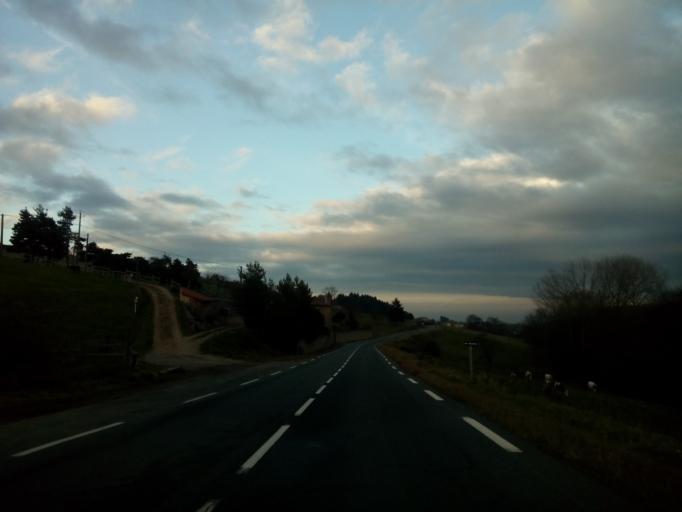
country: FR
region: Rhone-Alpes
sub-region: Departement de la Loire
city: Saint-Julien-Molin-Molette
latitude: 45.3138
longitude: 4.6042
